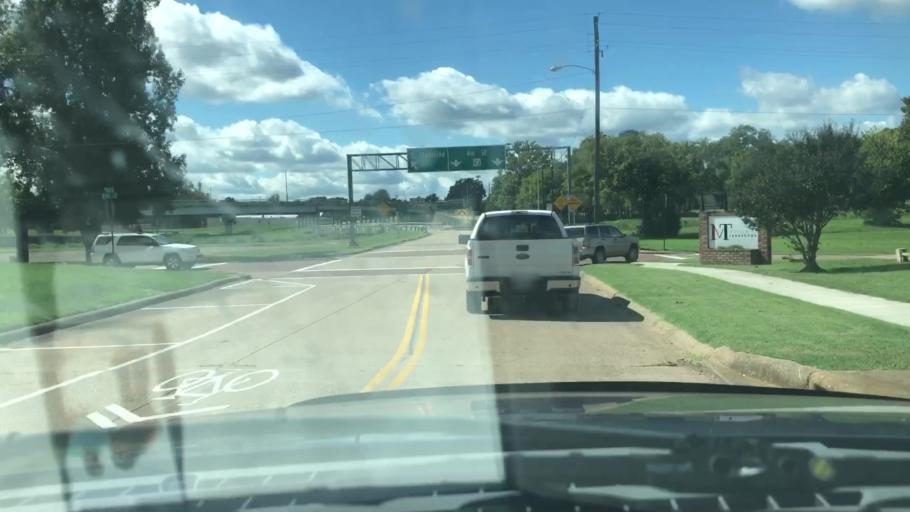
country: US
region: Texas
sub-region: Bowie County
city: Texarkana
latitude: 33.4211
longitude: -94.0493
